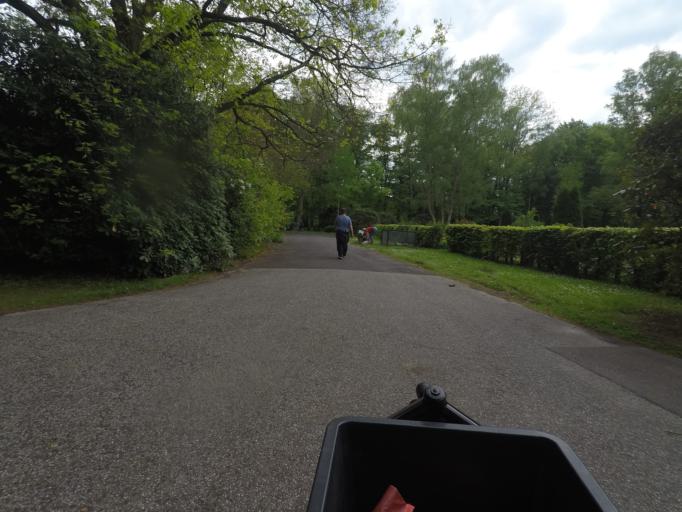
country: DE
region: Hamburg
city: Steilshoop
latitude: 53.6212
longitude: 10.0633
